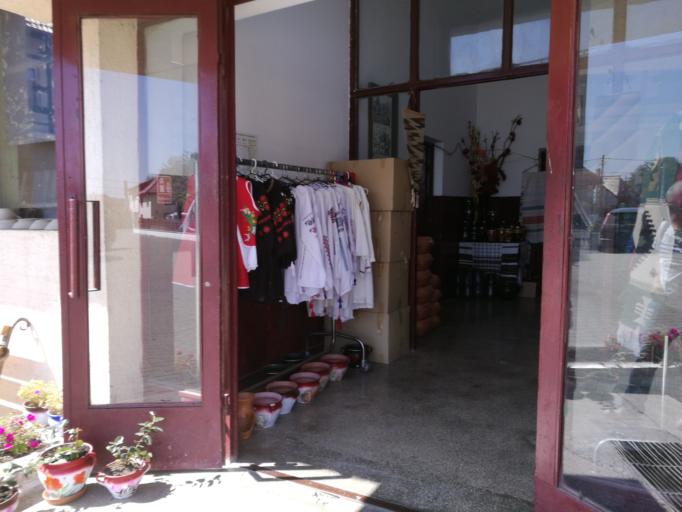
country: RO
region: Suceava
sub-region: Comuna Marginea
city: Marginea
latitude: 47.8014
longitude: 25.7941
